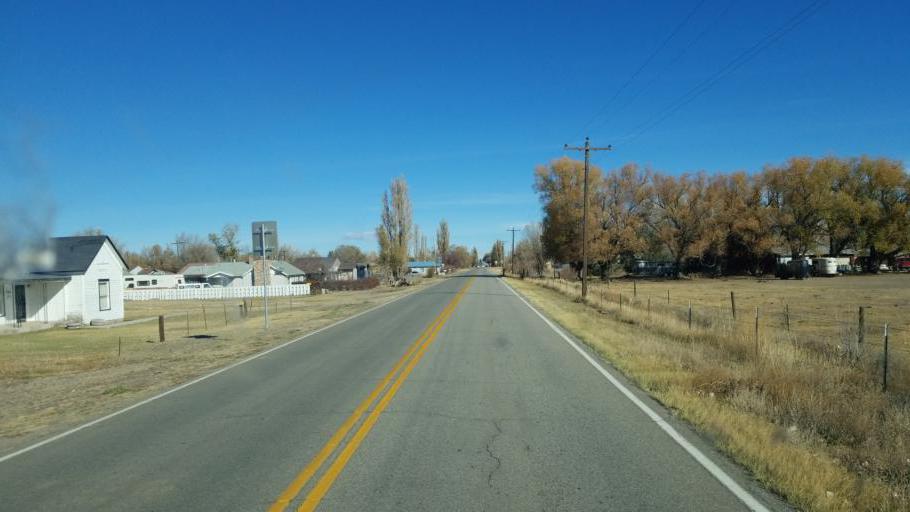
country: US
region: Colorado
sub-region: Rio Grande County
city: Monte Vista
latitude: 37.5697
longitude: -106.1495
